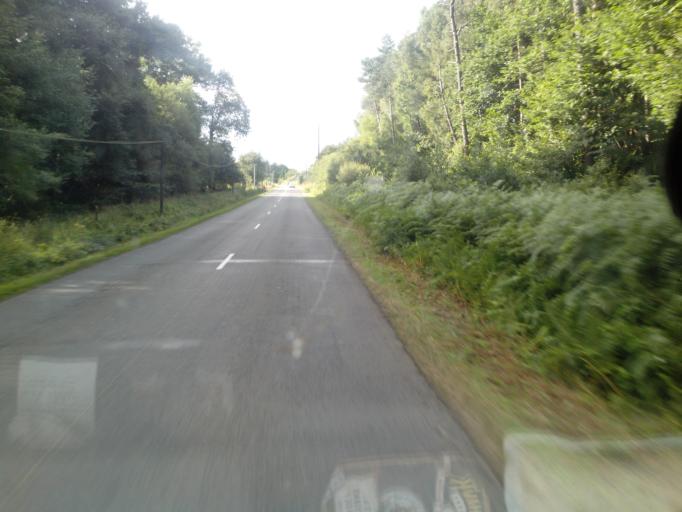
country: FR
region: Brittany
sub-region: Departement d'Ille-et-Vilaine
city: Paimpont
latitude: 48.0354
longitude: -2.1794
